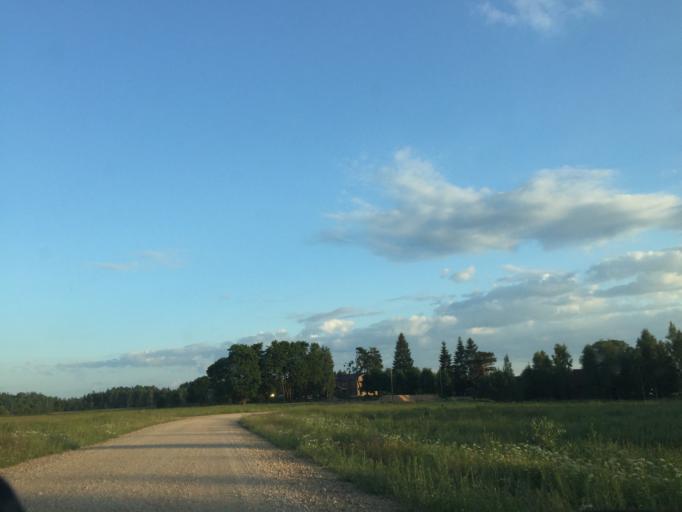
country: LV
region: Sigulda
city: Sigulda
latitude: 57.1184
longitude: 24.9584
